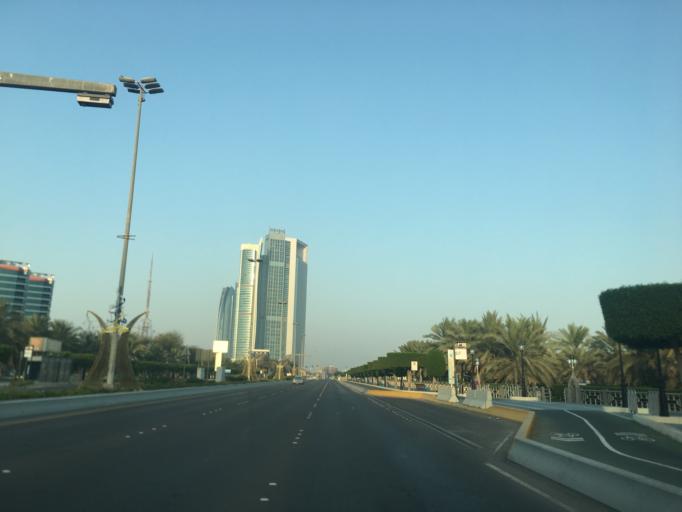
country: AE
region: Abu Dhabi
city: Abu Dhabi
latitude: 24.4700
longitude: 54.3357
